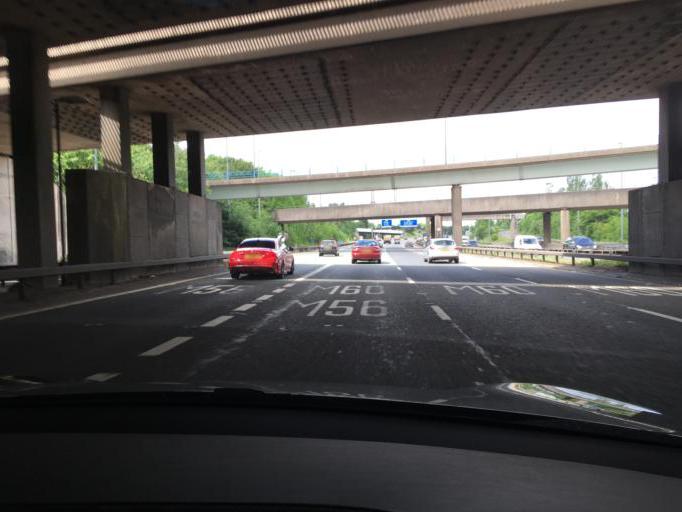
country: GB
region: England
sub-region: Manchester
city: Didsbury
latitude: 53.3988
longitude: -2.2261
